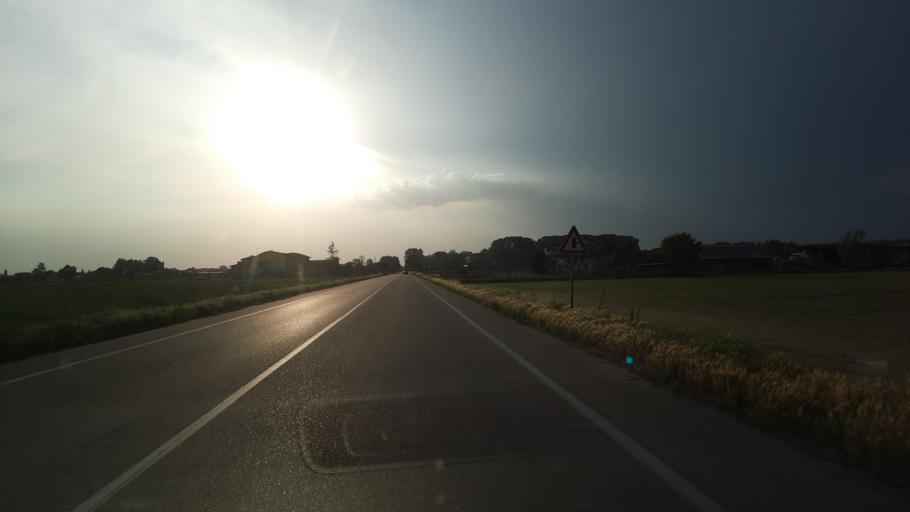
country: IT
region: Lombardy
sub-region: Provincia di Pavia
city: Mortara
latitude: 45.2457
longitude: 8.7670
